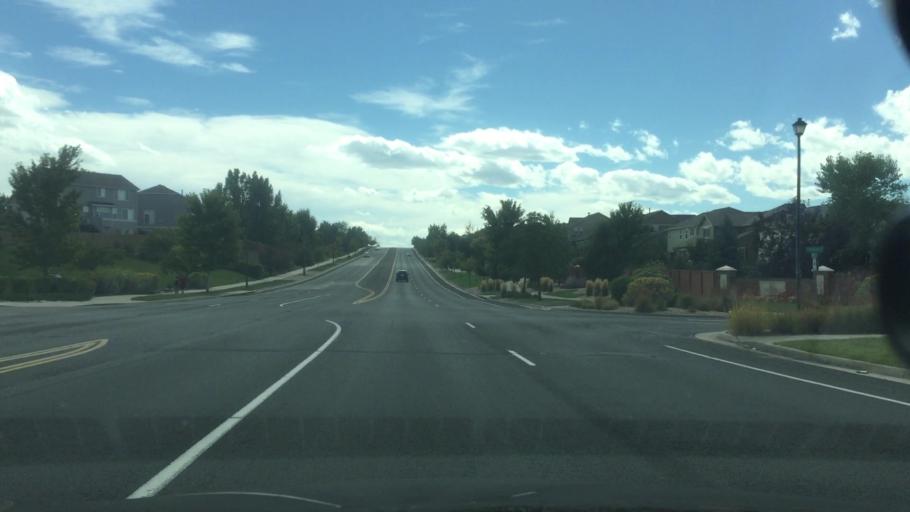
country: US
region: Colorado
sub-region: Arapahoe County
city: Dove Valley
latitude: 39.6467
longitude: -104.7351
